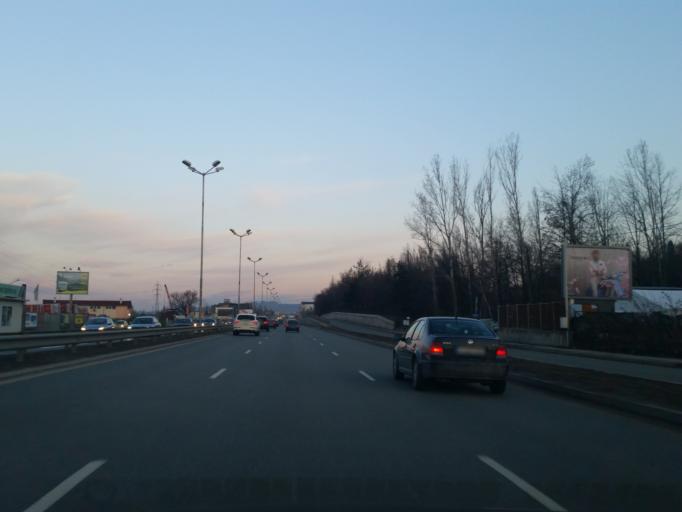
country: BG
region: Sofia-Capital
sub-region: Stolichna Obshtina
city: Sofia
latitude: 42.6484
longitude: 23.2958
